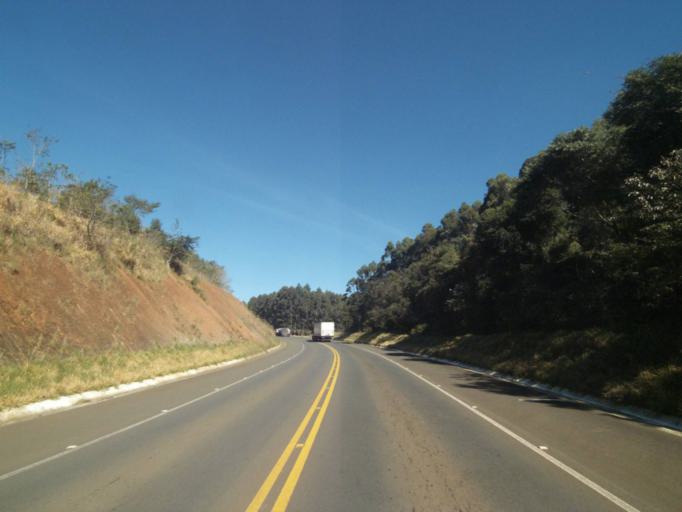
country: BR
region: Parana
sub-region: Tibagi
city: Tibagi
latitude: -24.7491
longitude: -50.4642
